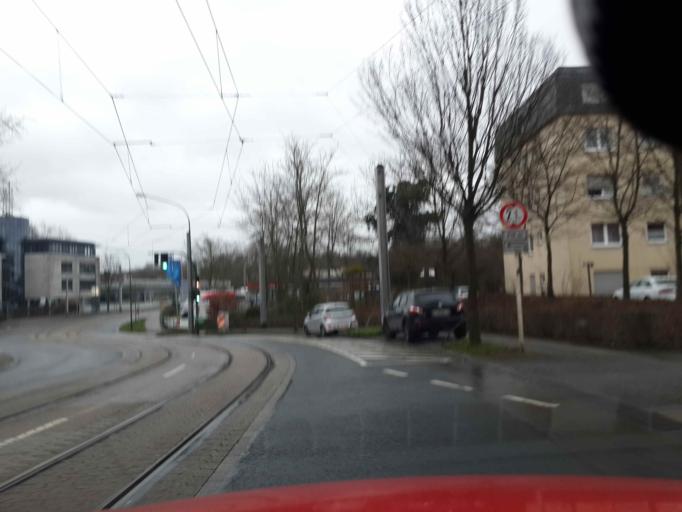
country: DE
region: North Rhine-Westphalia
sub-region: Regierungsbezirk Dusseldorf
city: Essen
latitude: 51.4293
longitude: 7.0406
